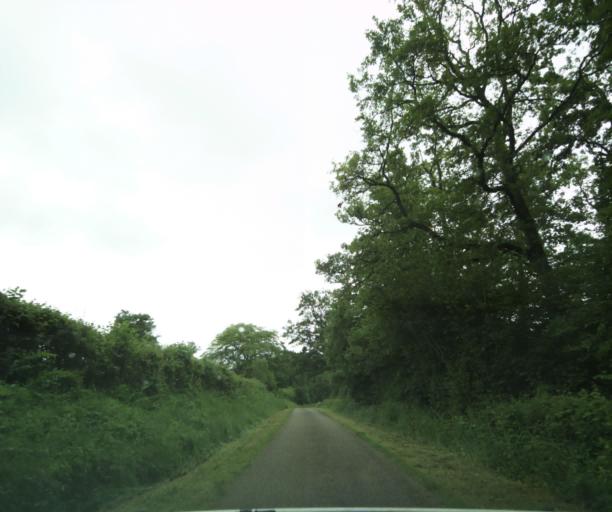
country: FR
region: Bourgogne
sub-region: Departement de Saone-et-Loire
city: Charolles
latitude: 46.4671
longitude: 4.2901
